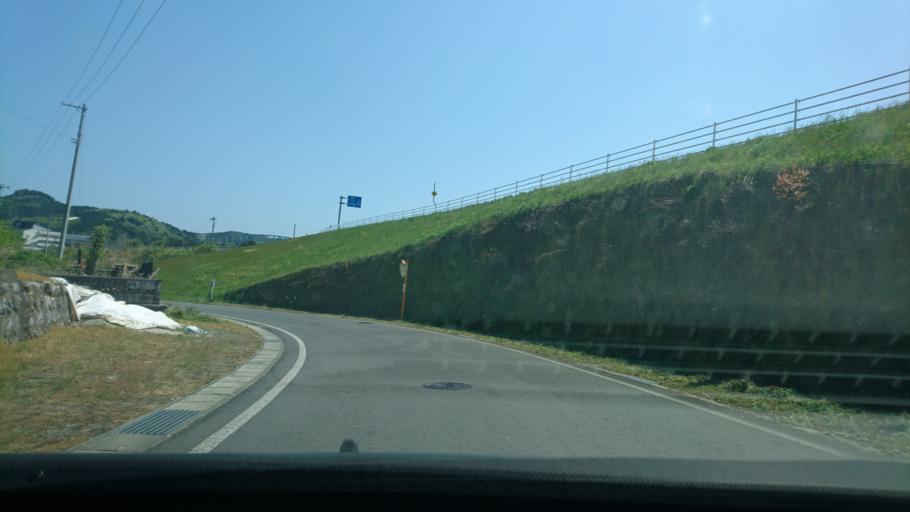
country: JP
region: Iwate
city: Ichinoseki
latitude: 38.9052
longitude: 141.2606
